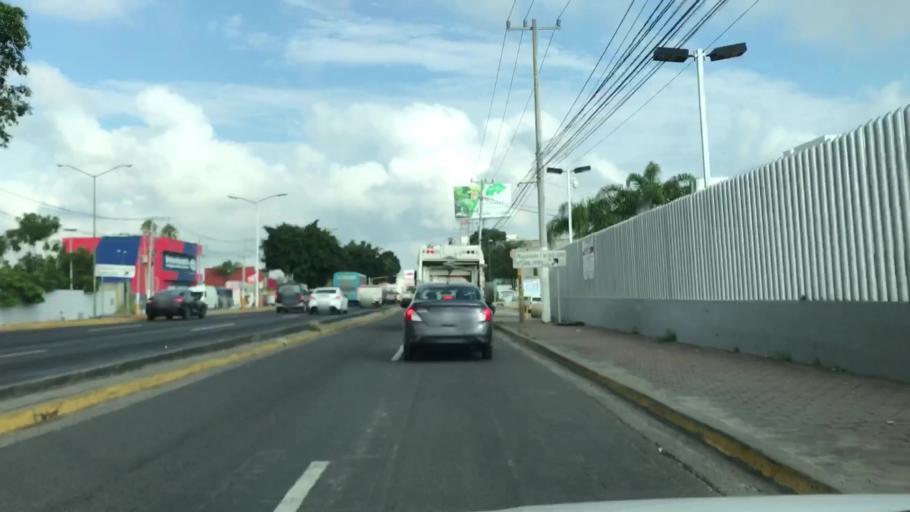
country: MX
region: Jalisco
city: Nuevo Mexico
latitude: 20.7567
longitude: -103.4286
